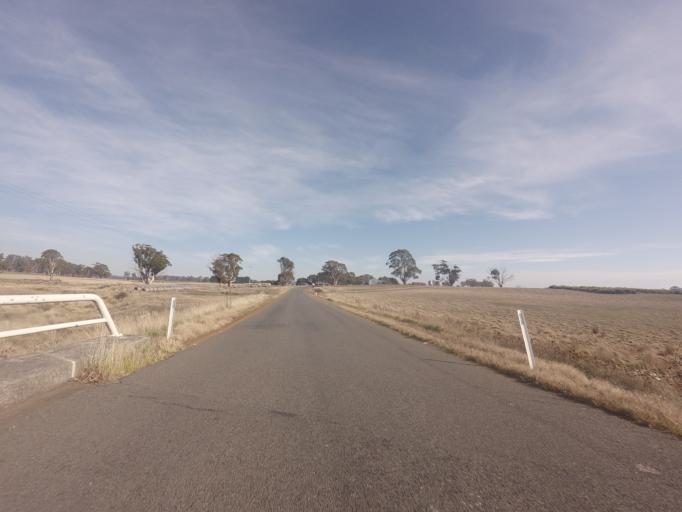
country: AU
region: Tasmania
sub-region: Sorell
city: Sorell
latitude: -42.4448
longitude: 147.4675
